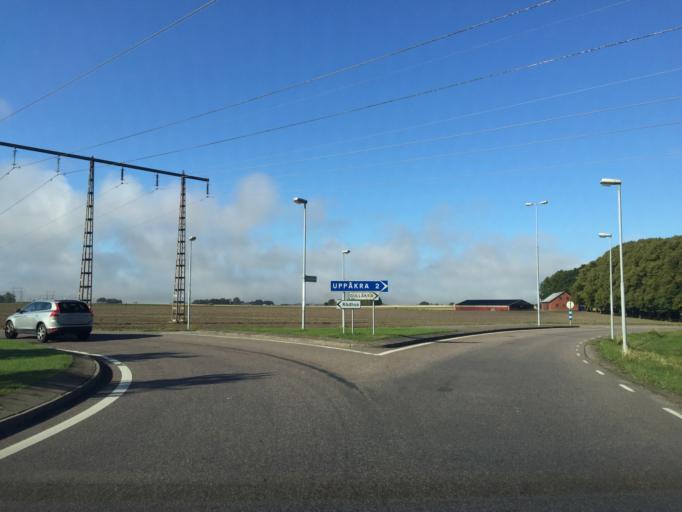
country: SE
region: Skane
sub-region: Staffanstorps Kommun
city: Staffanstorp
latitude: 55.6532
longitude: 13.2026
